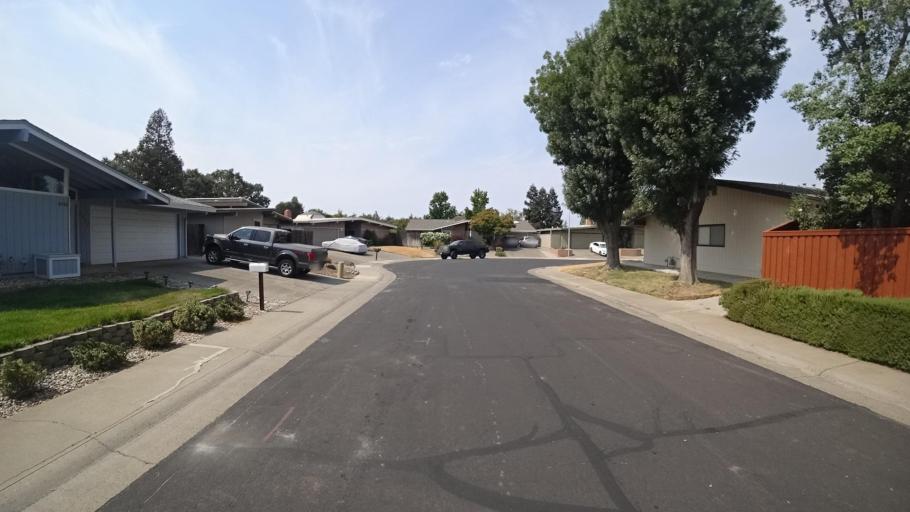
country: US
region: California
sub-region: Sacramento County
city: Elk Grove
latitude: 38.4109
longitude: -121.3802
